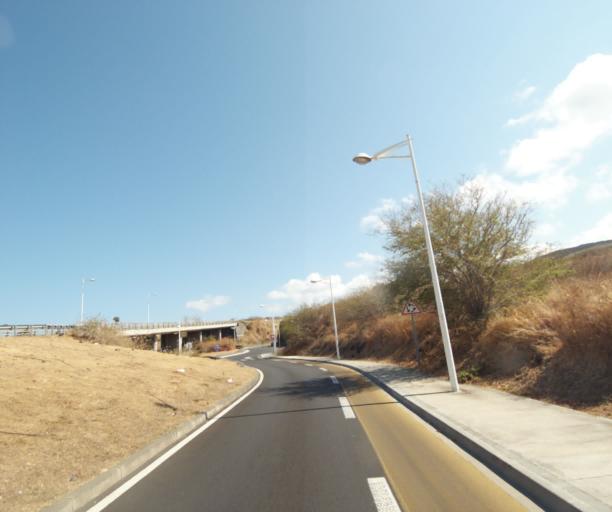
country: RE
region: Reunion
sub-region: Reunion
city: Trois-Bassins
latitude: -21.1035
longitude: 55.2482
